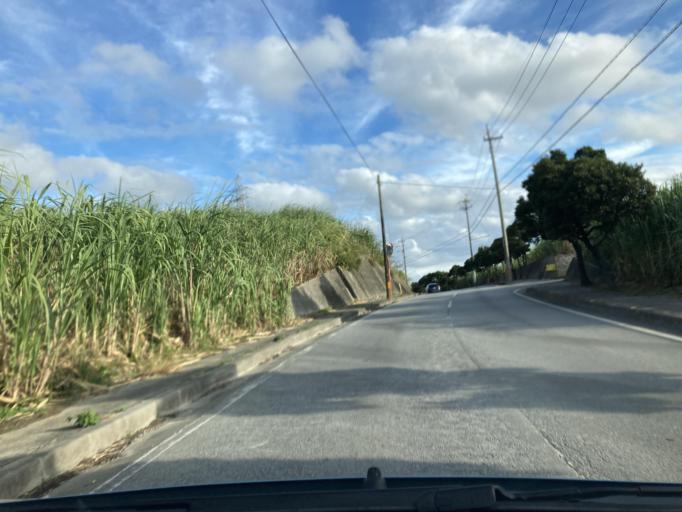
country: JP
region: Okinawa
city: Tomigusuku
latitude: 26.1581
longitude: 127.7382
